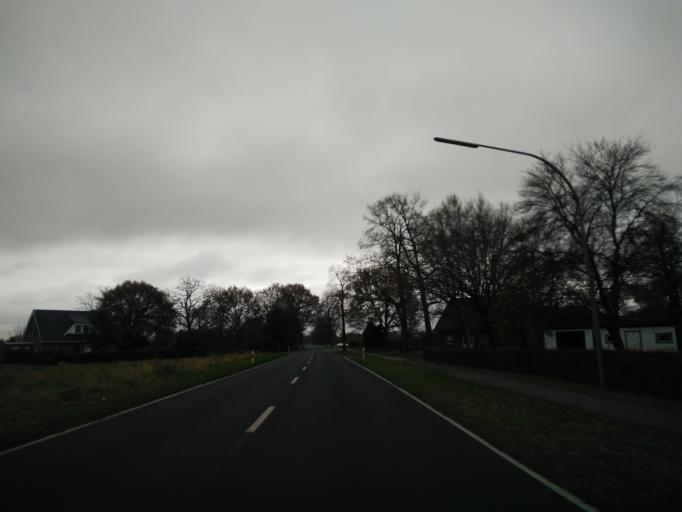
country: NL
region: Drenthe
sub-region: Gemeente Emmen
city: Emmer-Compascuum
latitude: 52.8285
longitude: 7.1068
